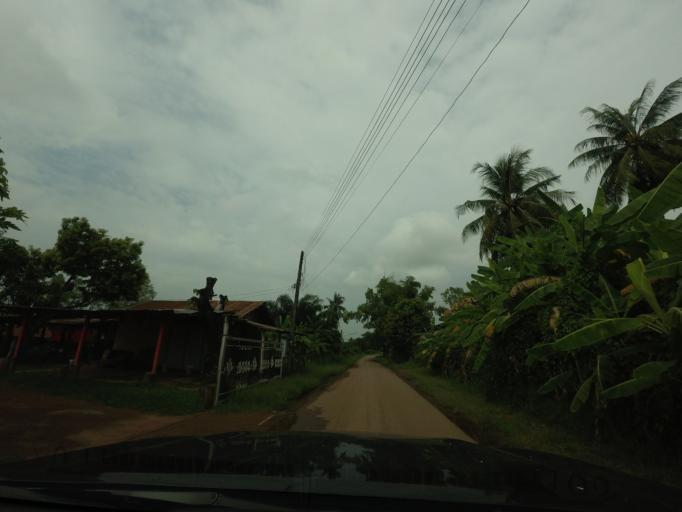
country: TH
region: Nong Khai
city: Nong Khai
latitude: 17.8171
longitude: 102.7112
